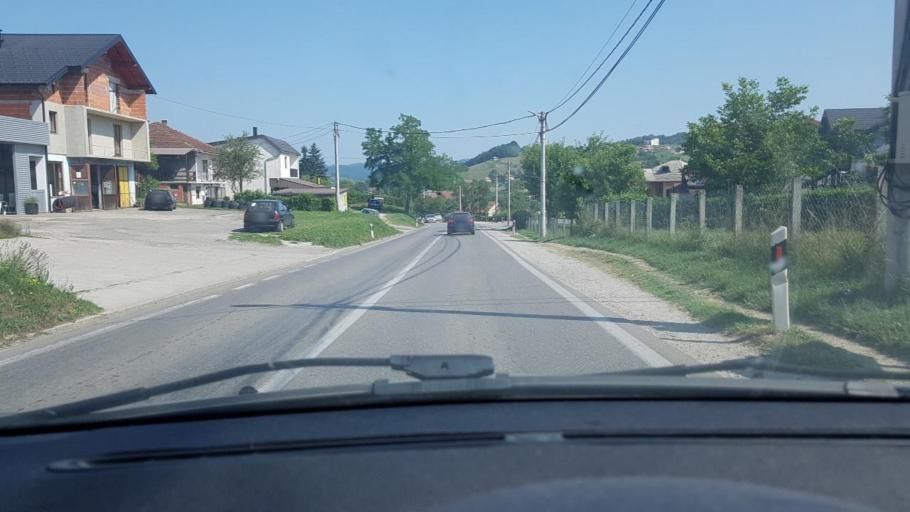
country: BA
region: Federation of Bosnia and Herzegovina
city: Velika Kladusa
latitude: 45.1767
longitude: 15.8213
